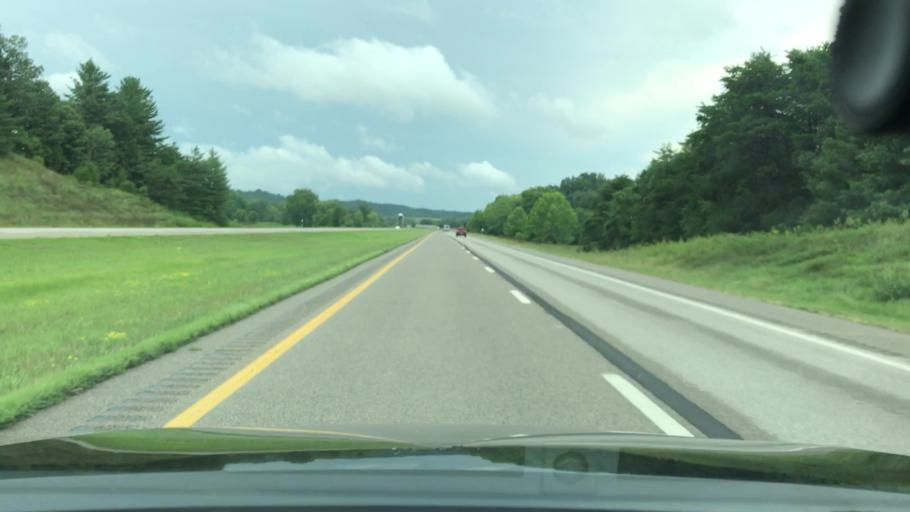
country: US
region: Ohio
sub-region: Gallia County
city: Gallipolis
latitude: 38.8656
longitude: -82.2653
